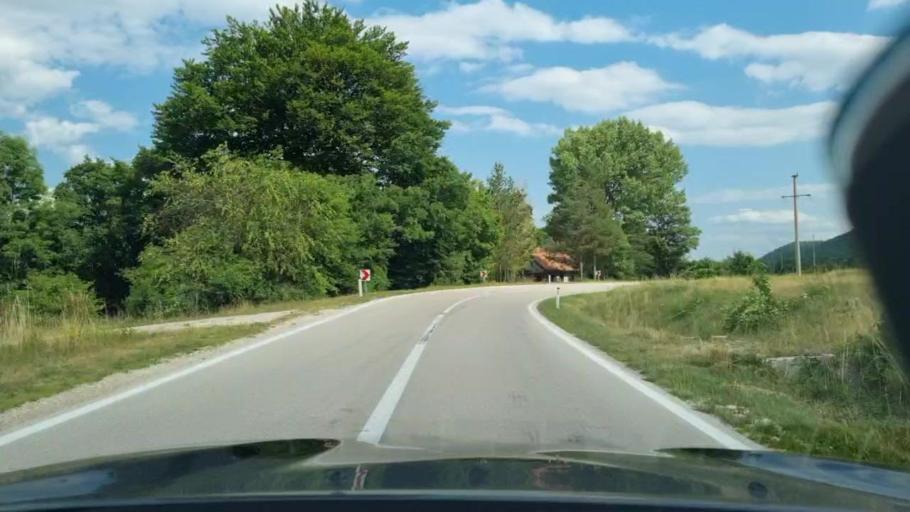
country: HR
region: Splitsko-Dalmatinska
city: Hrvace
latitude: 44.0023
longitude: 16.6075
